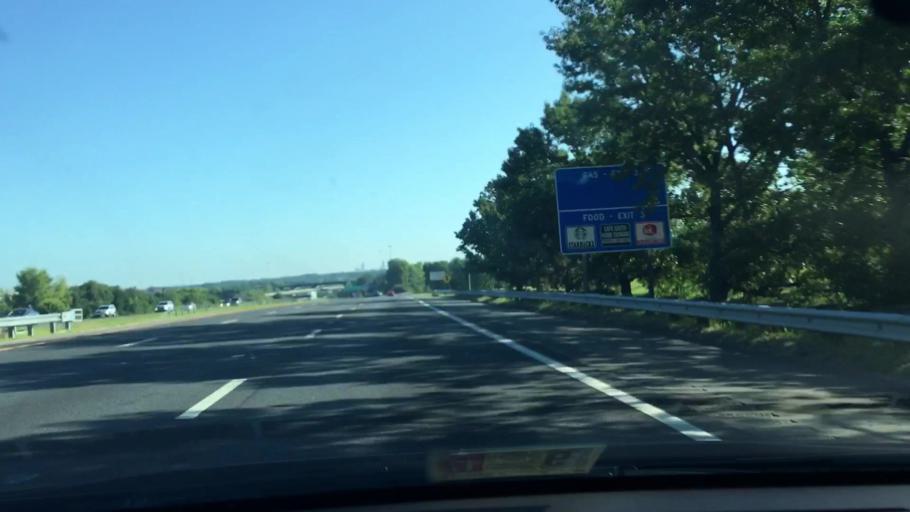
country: US
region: North Carolina
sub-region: Mecklenburg County
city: Pineville
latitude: 35.1154
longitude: -80.9232
